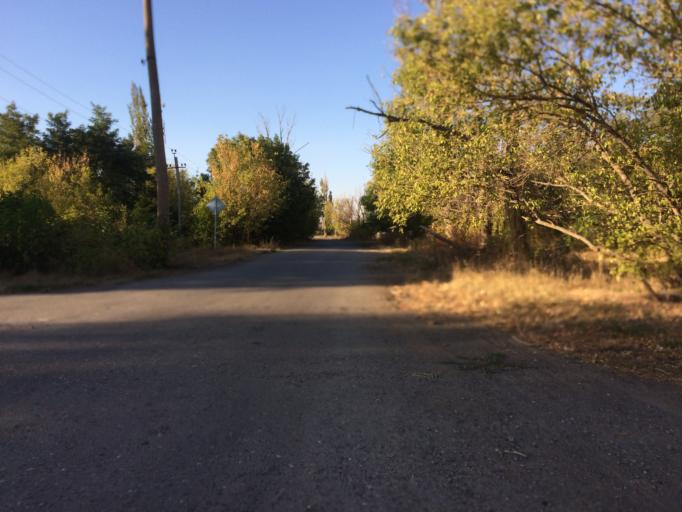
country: RU
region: Rostov
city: Gigant
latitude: 46.5154
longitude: 41.1922
